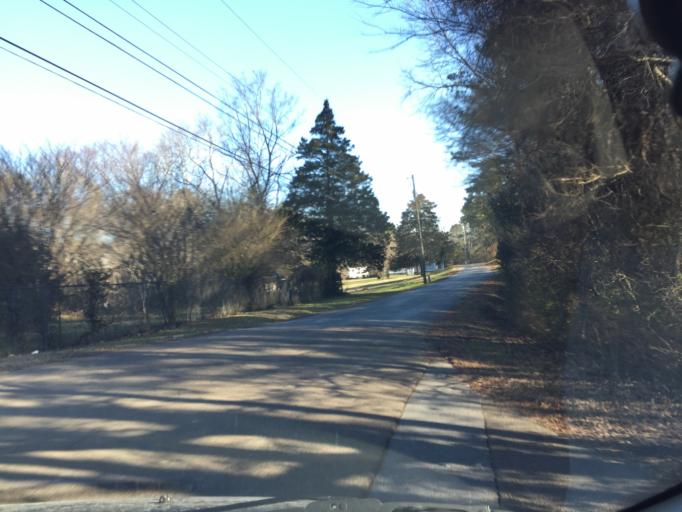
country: US
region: Tennessee
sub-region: Hamilton County
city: Collegedale
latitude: 35.0720
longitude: -85.1018
